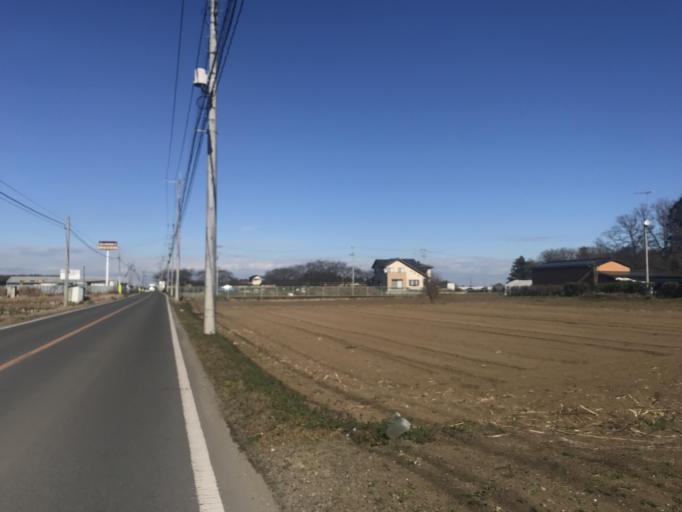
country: JP
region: Ibaraki
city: Yuki
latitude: 36.3590
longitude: 139.8767
